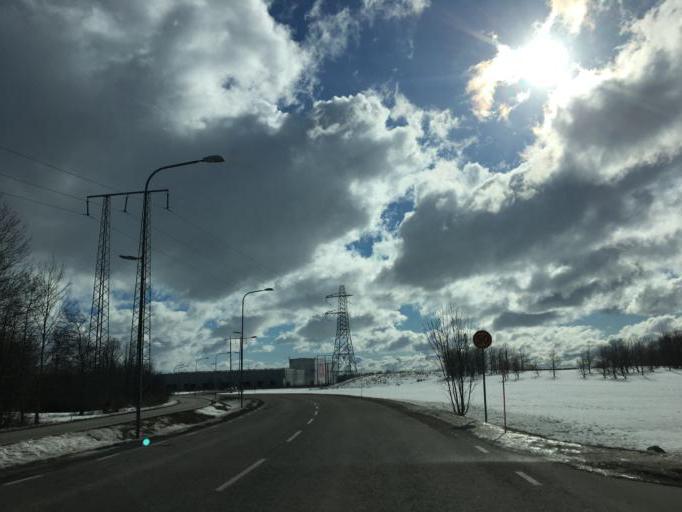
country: SE
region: Vaestmanland
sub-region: Vasteras
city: Vasteras
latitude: 59.5931
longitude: 16.4672
